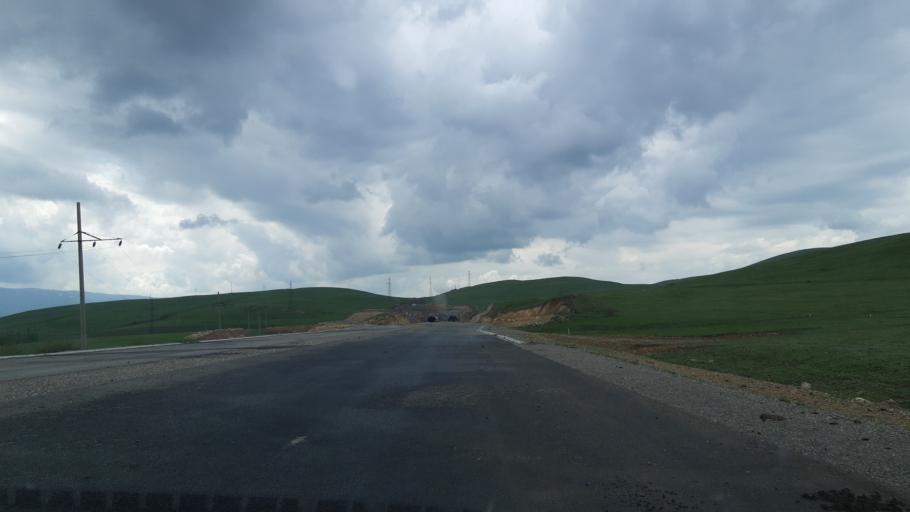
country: KZ
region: Ongtustik Qazaqstan
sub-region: Tulkibas Audany
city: Zhabagly
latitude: 42.5237
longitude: 70.5867
